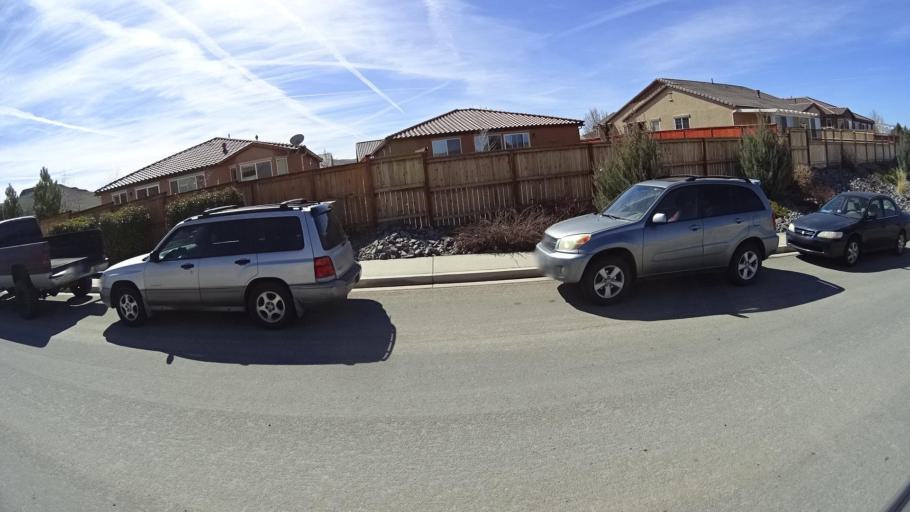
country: US
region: Nevada
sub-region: Washoe County
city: Spanish Springs
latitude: 39.5828
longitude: -119.6897
